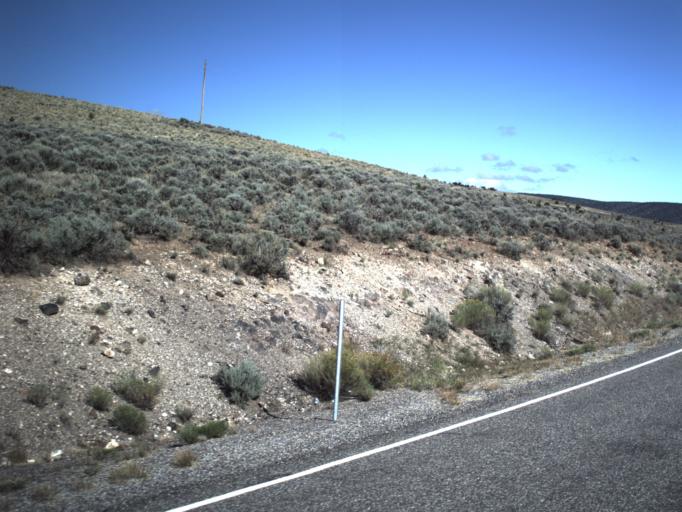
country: US
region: Utah
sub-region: Sevier County
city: Monroe
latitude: 38.5390
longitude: -111.8727
